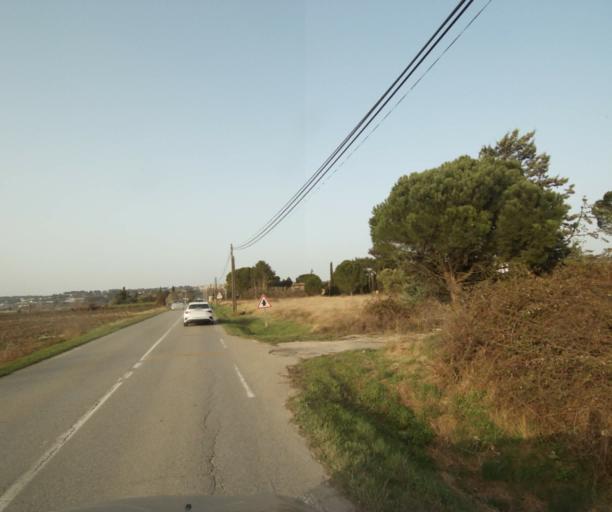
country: FR
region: Provence-Alpes-Cote d'Azur
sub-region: Departement des Bouches-du-Rhone
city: Eguilles
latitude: 43.5490
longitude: 5.3492
